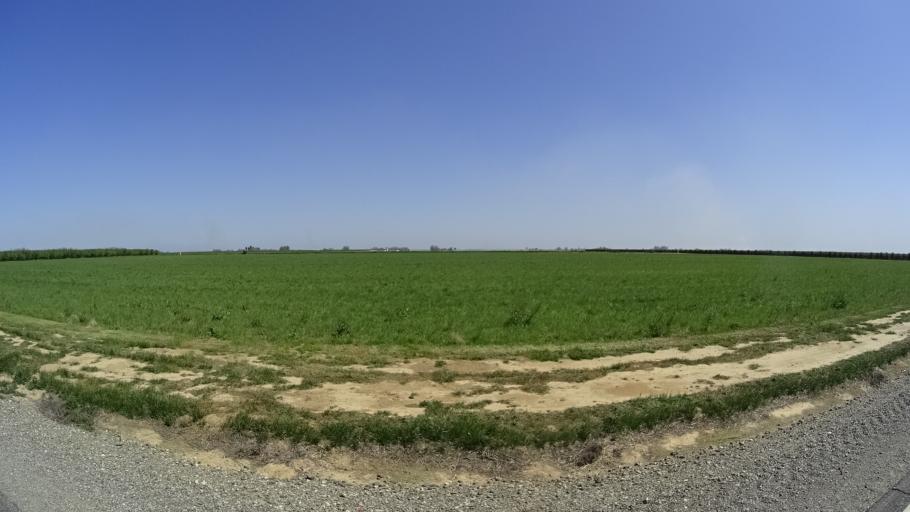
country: US
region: California
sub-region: Glenn County
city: Willows
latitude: 39.5692
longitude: -122.1373
